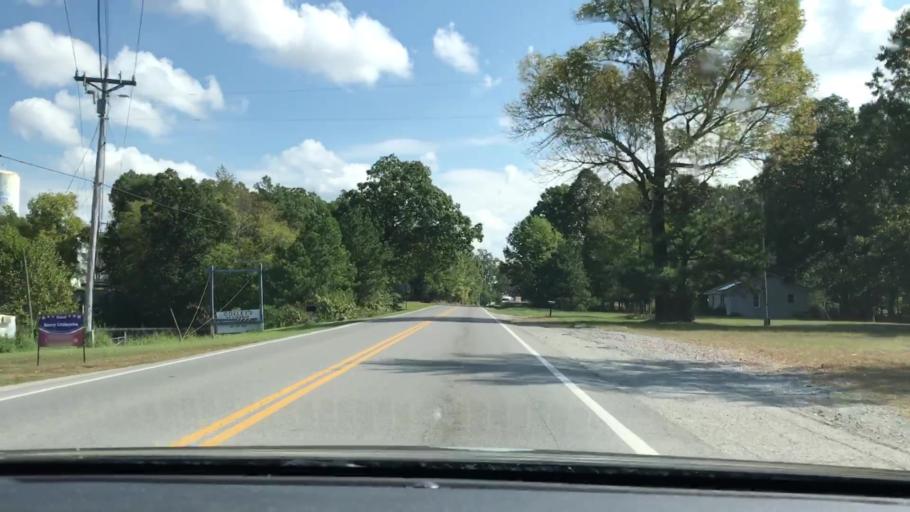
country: US
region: Kentucky
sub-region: Trigg County
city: Cadiz
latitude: 36.8111
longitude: -87.8952
